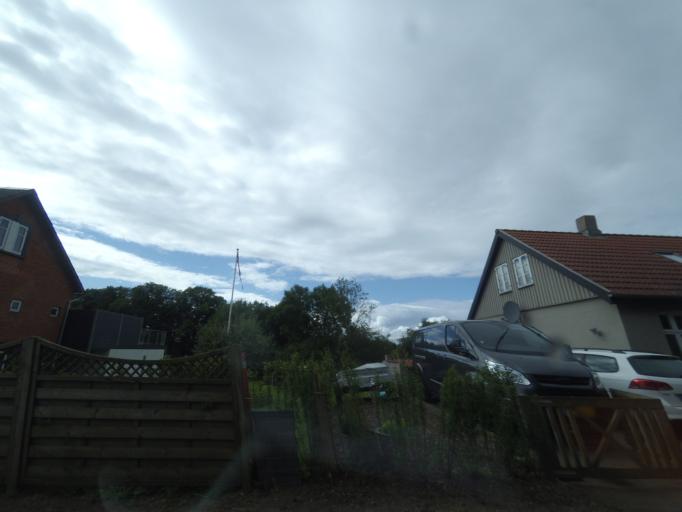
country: DK
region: South Denmark
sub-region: Nordfyns Kommune
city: Sonderso
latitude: 55.4720
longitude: 10.2145
